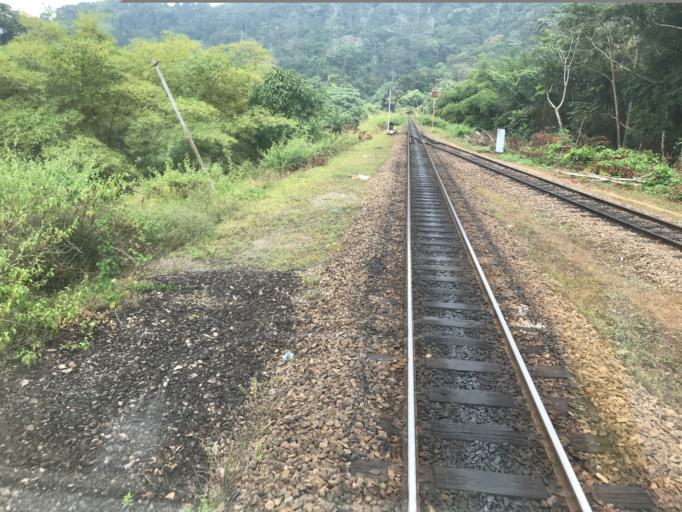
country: CM
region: Centre
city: Eseka
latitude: 3.5754
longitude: 10.8996
